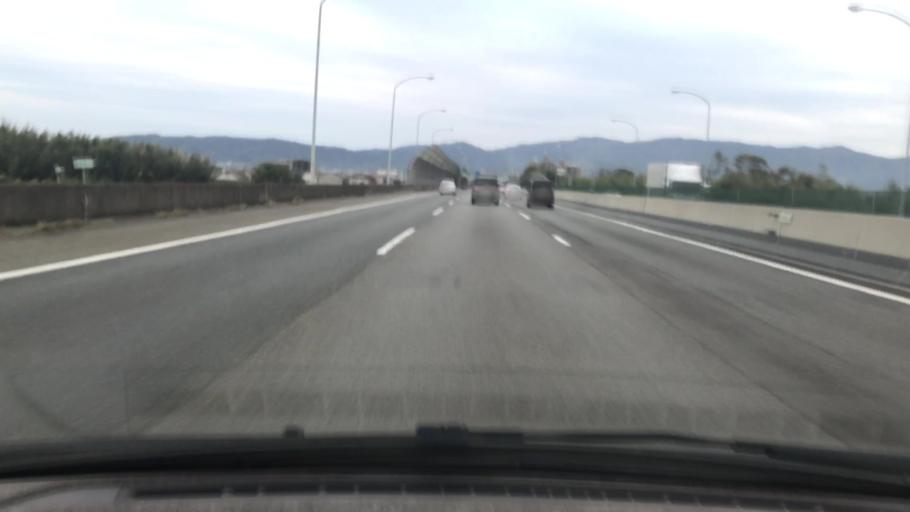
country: JP
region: Kyoto
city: Muko
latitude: 34.9502
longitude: 135.7356
